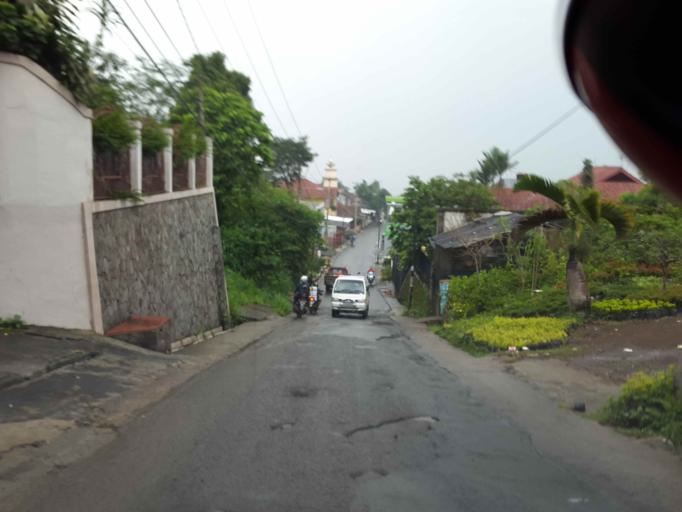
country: ID
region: West Java
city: Cimahi
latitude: -6.8514
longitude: 107.5810
